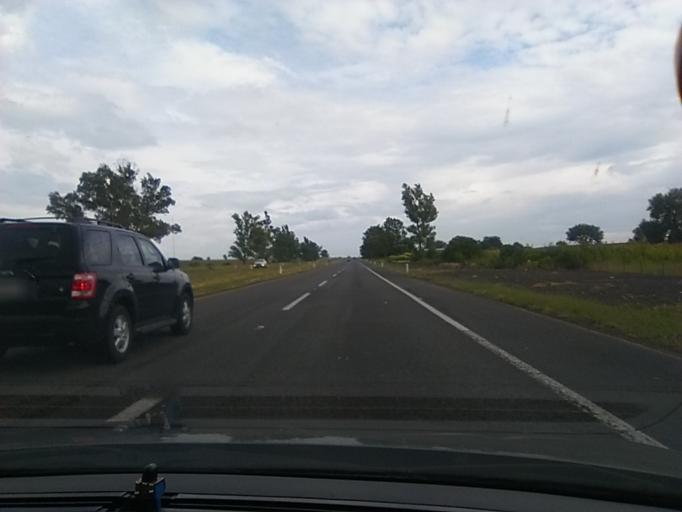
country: MX
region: Jalisco
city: Jamay
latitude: 20.3565
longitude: -102.6401
